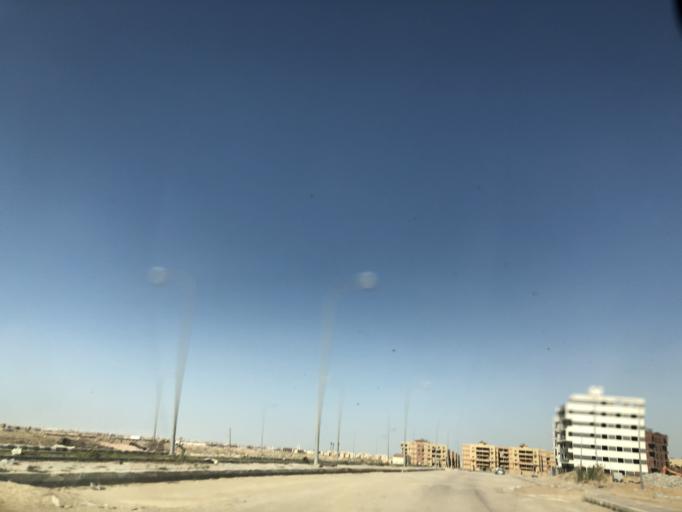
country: EG
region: Al Jizah
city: Madinat Sittah Uktubar
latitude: 29.9253
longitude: 31.0389
